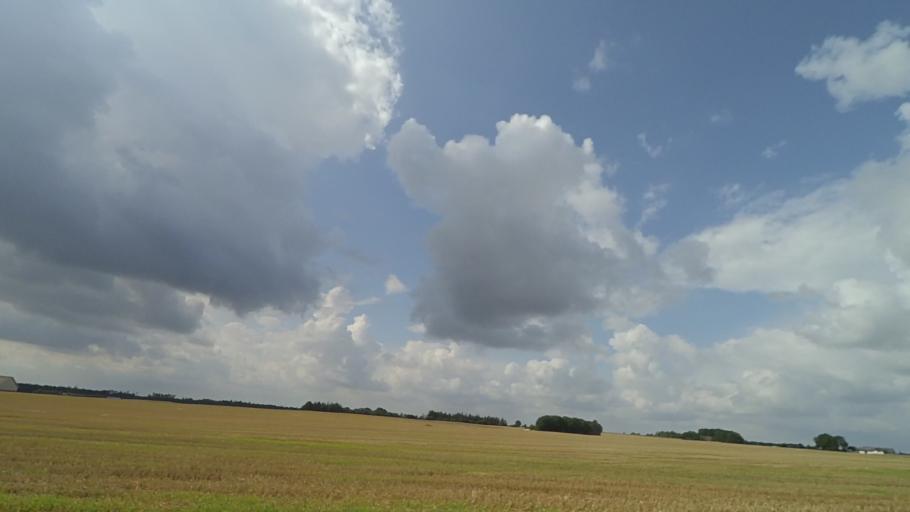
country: DK
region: Central Jutland
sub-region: Norddjurs Kommune
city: Allingabro
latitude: 56.5042
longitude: 10.3714
